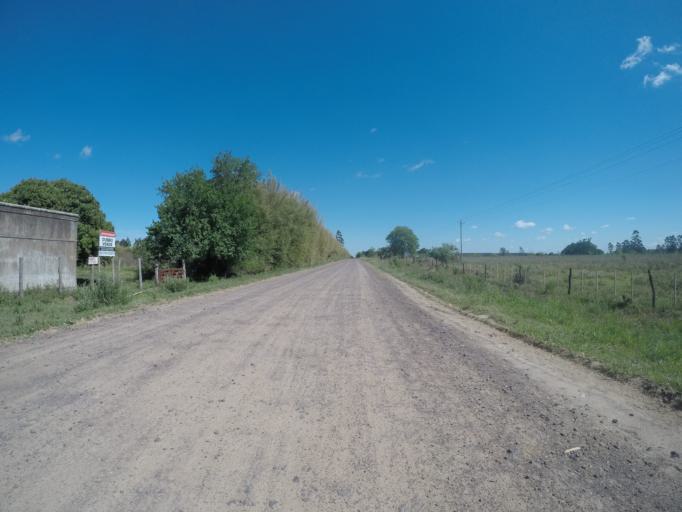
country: AR
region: Corrientes
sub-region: Departamento de San Roque
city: San Roque
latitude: -28.5279
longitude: -58.4936
